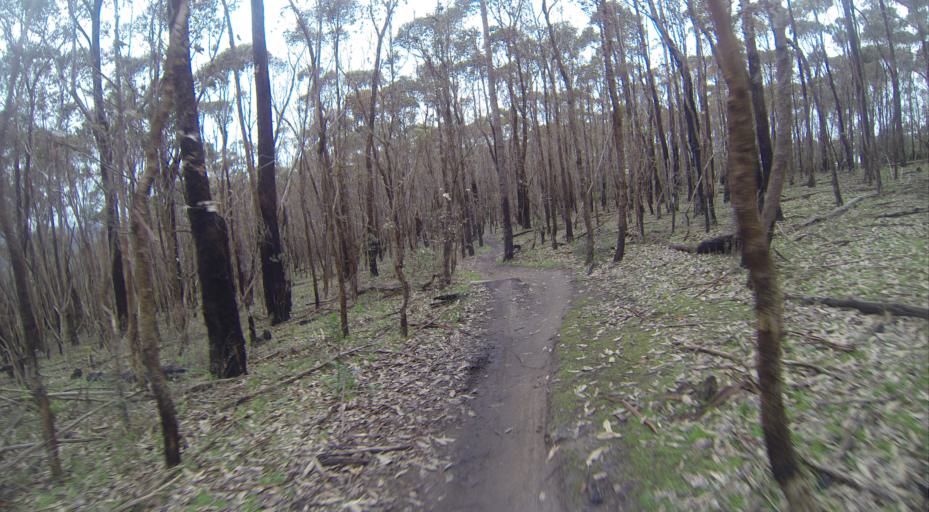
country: AU
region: Victoria
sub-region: Yarra Ranges
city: Lysterfield
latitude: -37.9559
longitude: 145.2867
